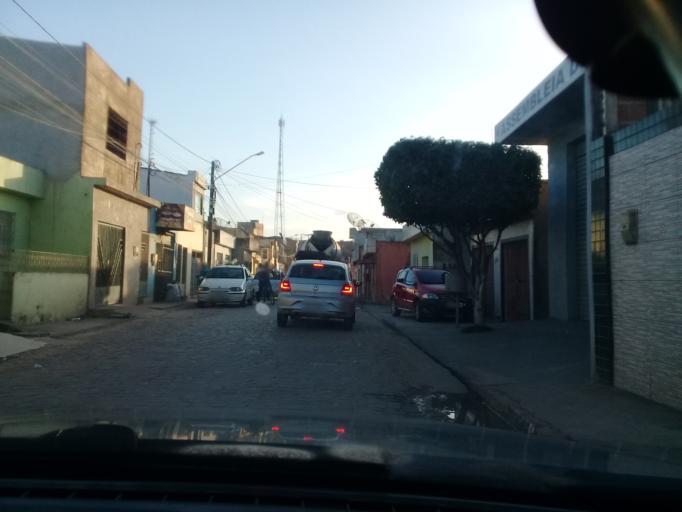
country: BR
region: Pernambuco
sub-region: Vitoria De Santo Antao
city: Vitoria de Santo Antao
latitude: -8.1282
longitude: -35.2854
